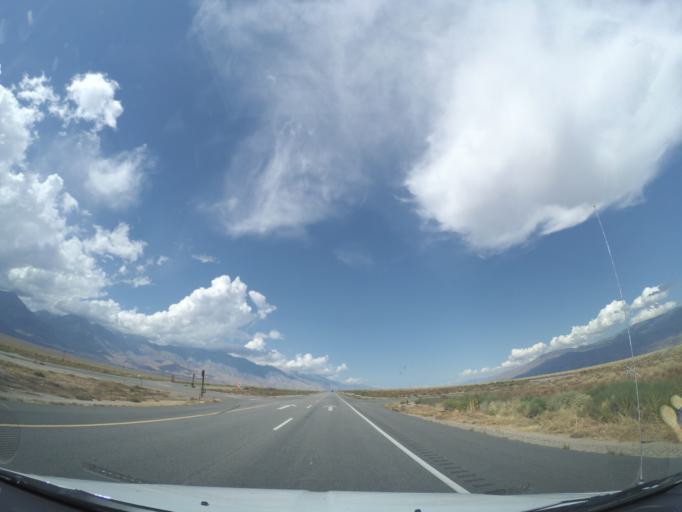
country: US
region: California
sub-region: Inyo County
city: Lone Pine
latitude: 36.7579
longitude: -118.1669
